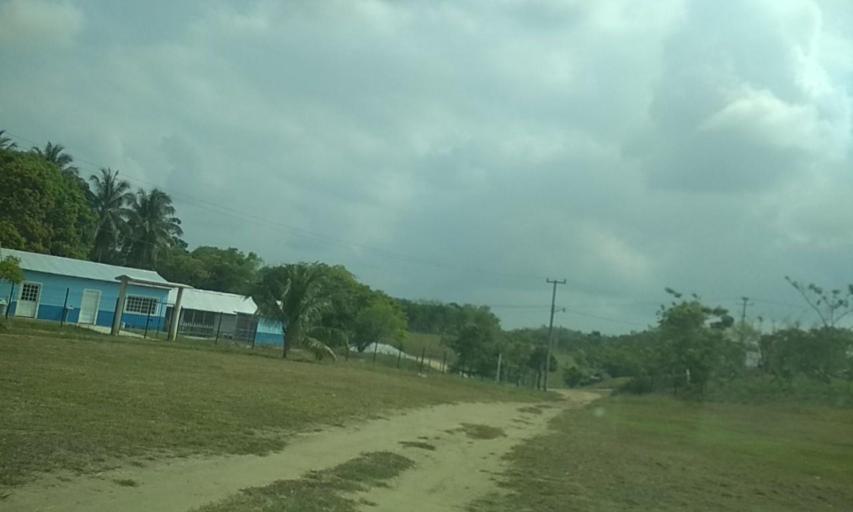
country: MX
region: Tabasco
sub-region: Huimanguillo
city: Francisco Rueda
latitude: 17.6545
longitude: -93.7547
